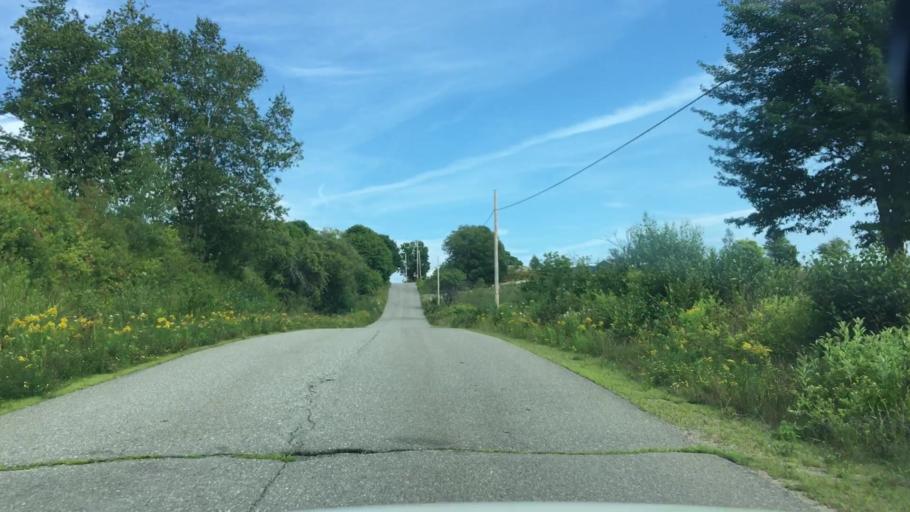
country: US
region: Maine
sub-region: Washington County
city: Eastport
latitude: 44.9068
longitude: -67.0007
